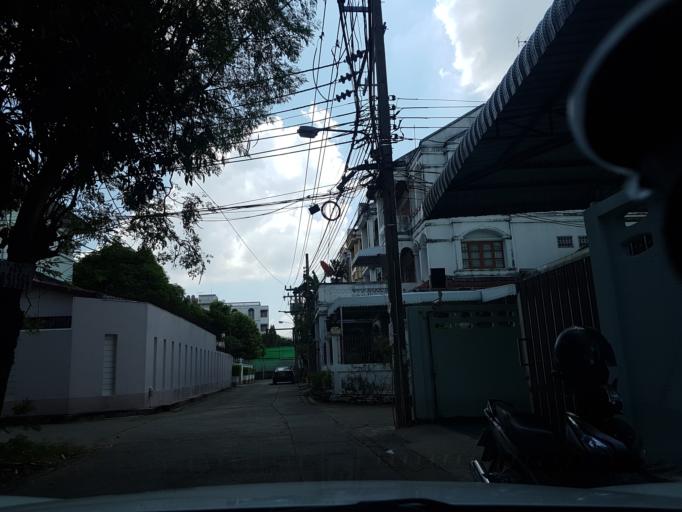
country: TH
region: Bangkok
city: Watthana
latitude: 13.7204
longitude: 100.5936
